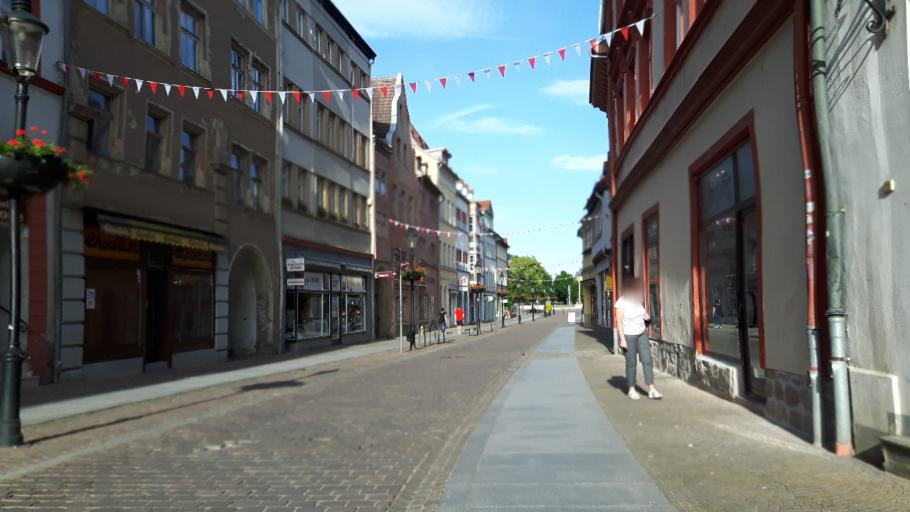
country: DE
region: Saxony-Anhalt
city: Naumburg
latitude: 51.1523
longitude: 11.8116
